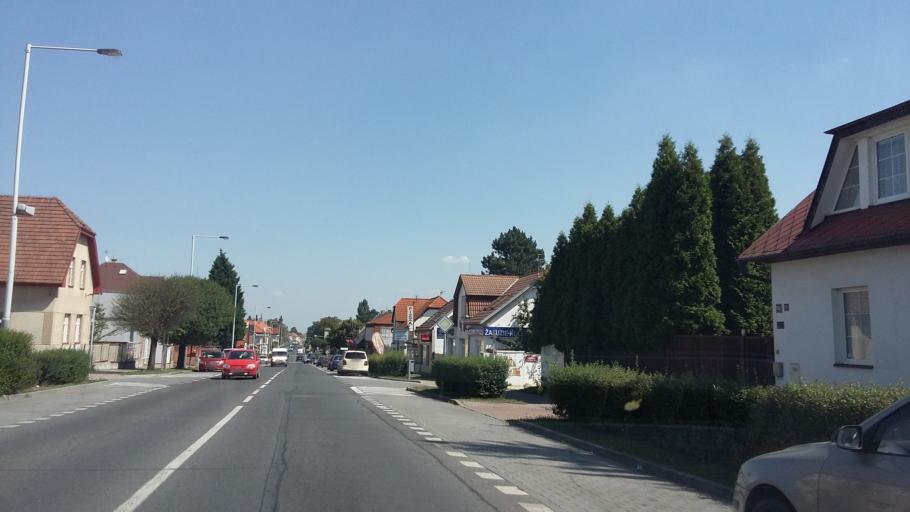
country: CZ
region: Praha
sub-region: Praha 20
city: Horni Pocernice
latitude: 50.1156
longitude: 14.6142
